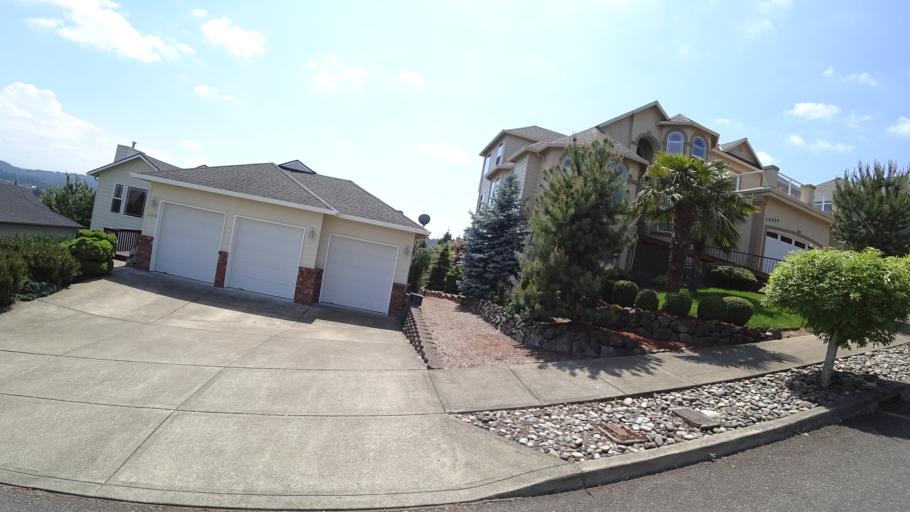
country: US
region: Oregon
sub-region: Clackamas County
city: Happy Valley
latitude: 45.4716
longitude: -122.5013
